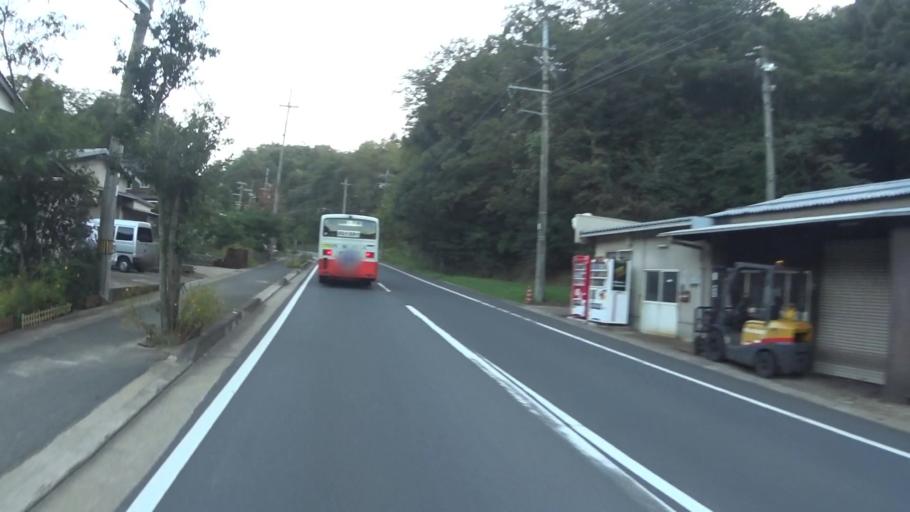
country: JP
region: Kyoto
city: Miyazu
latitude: 35.6355
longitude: 135.0540
